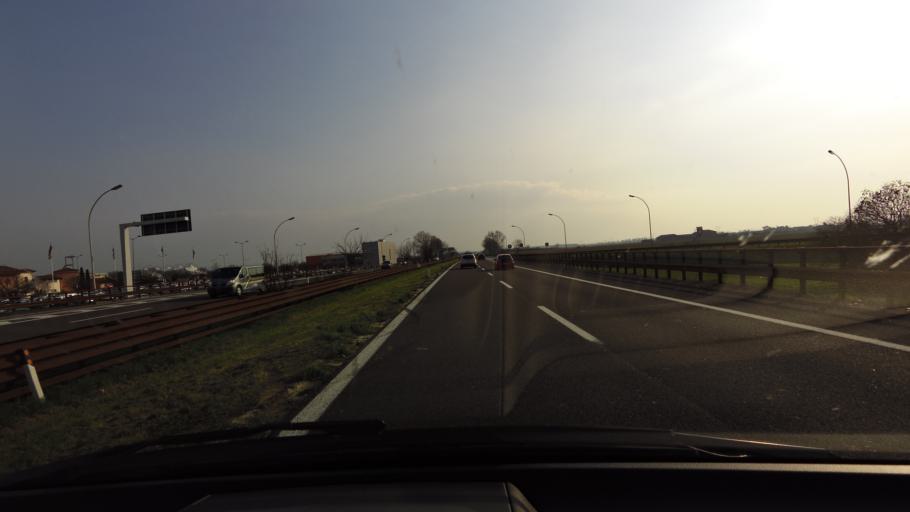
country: IT
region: Lombardy
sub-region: Provincia di Mantova
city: San Biagio
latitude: 45.0891
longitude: 10.8546
